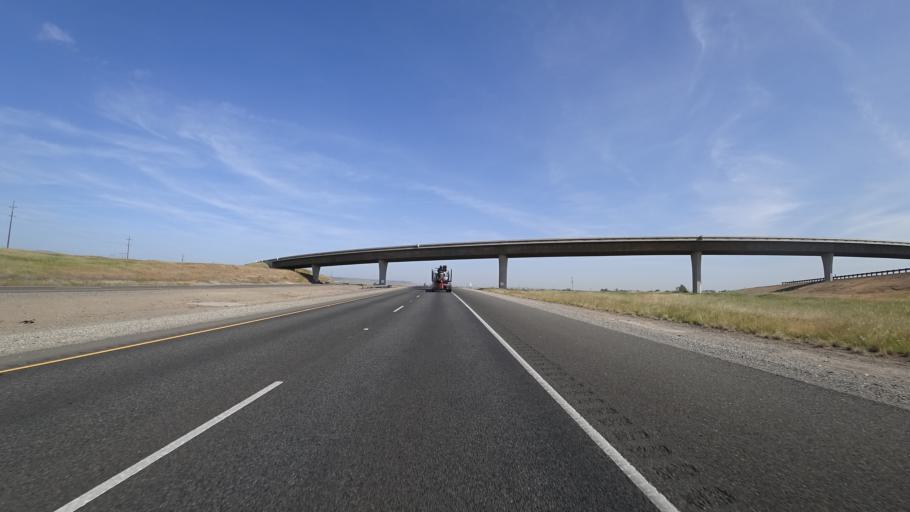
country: US
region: California
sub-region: Butte County
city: Durham
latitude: 39.6214
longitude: -121.6925
